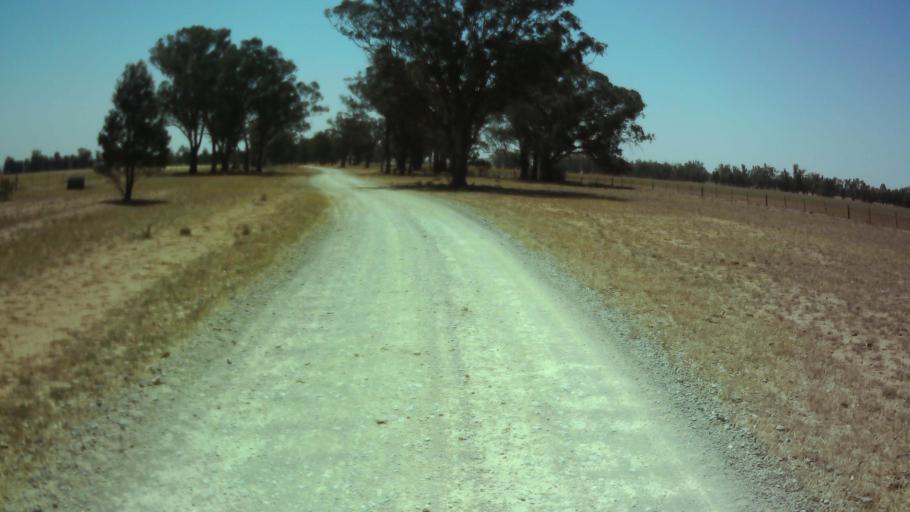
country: AU
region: New South Wales
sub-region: Weddin
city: Grenfell
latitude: -34.0199
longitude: 147.9002
